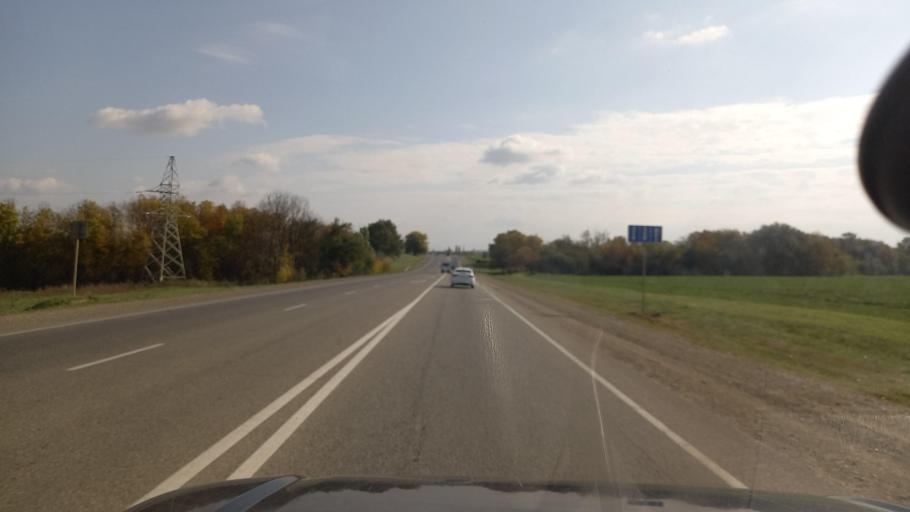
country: RU
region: Krasnodarskiy
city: Kholmskiy
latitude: 44.8544
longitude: 38.3539
